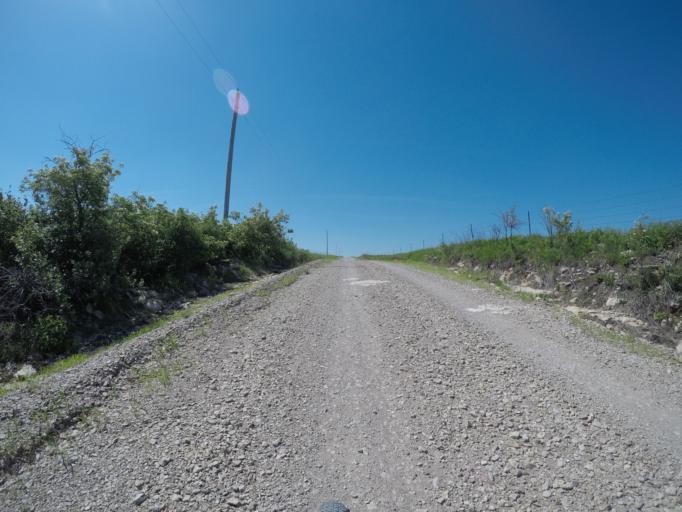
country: US
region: Kansas
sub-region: Wabaunsee County
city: Alma
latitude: 39.0134
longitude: -96.1784
